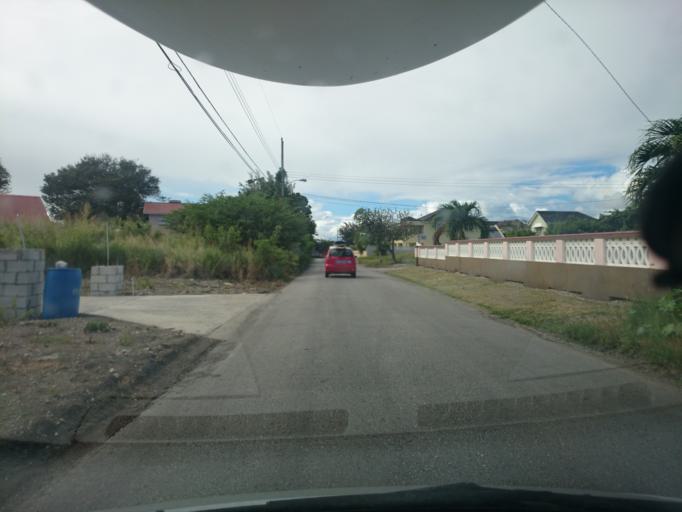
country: BB
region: Christ Church
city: Oistins
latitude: 13.0529
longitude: -59.5334
